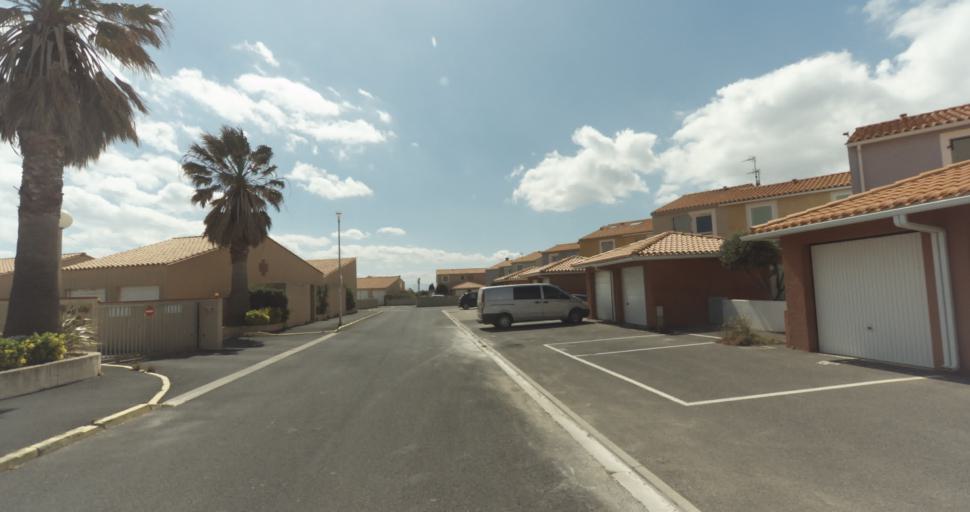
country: FR
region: Languedoc-Roussillon
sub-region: Departement de l'Aude
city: Leucate
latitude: 42.8761
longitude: 3.0468
